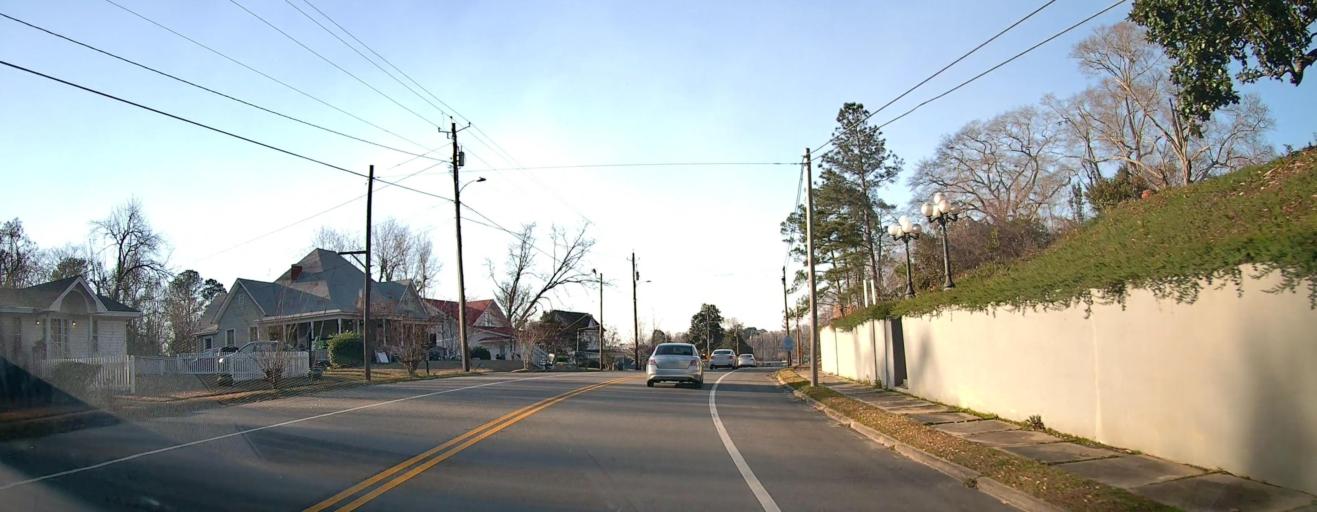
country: US
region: Georgia
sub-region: Meriwether County
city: Manchester
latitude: 32.8883
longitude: -84.6778
